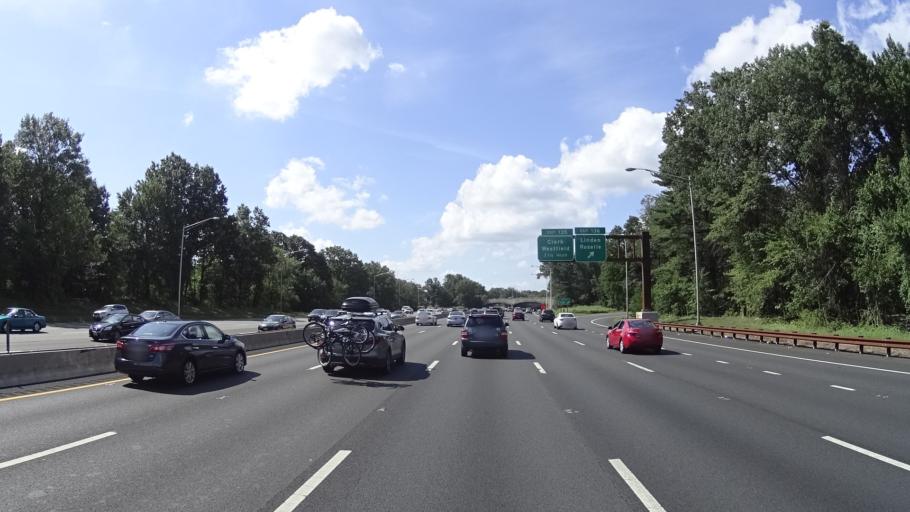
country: US
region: New Jersey
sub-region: Union County
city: Winfield
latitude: 40.6450
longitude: -74.2879
